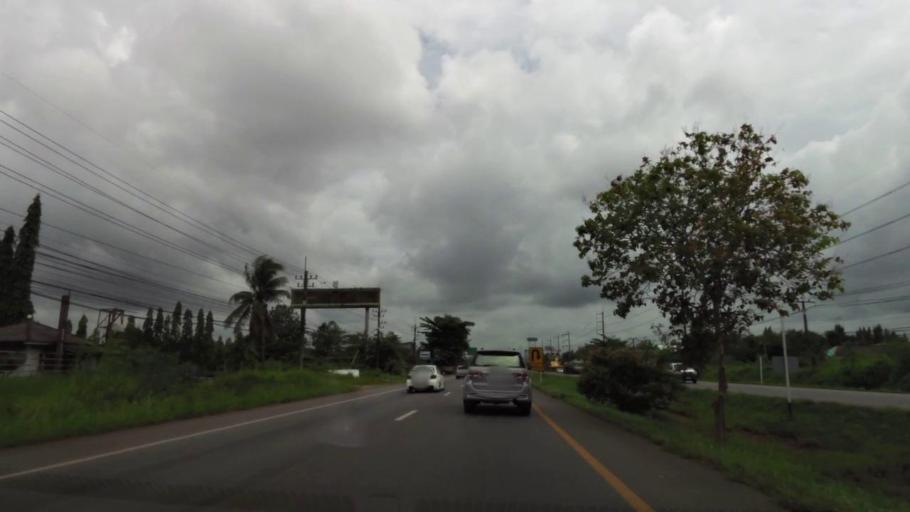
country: TH
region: Chanthaburi
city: Na Yai Am
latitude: 12.7639
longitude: 101.8530
